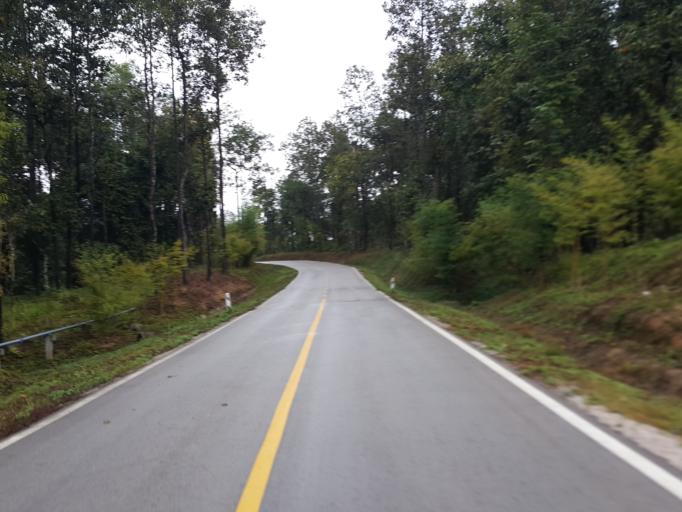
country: TH
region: Lampang
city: Hang Chat
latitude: 18.3564
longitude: 99.2442
